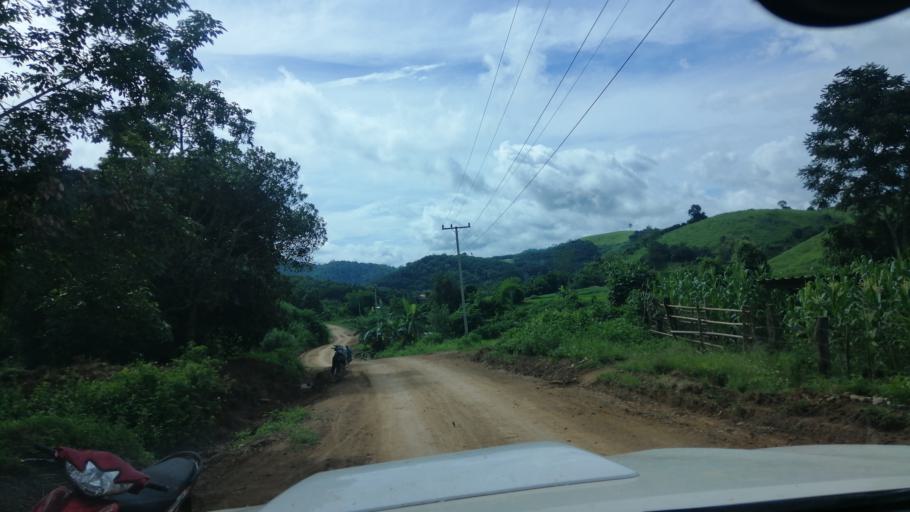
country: TH
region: Phayao
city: Phu Sang
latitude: 19.6362
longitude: 100.5269
